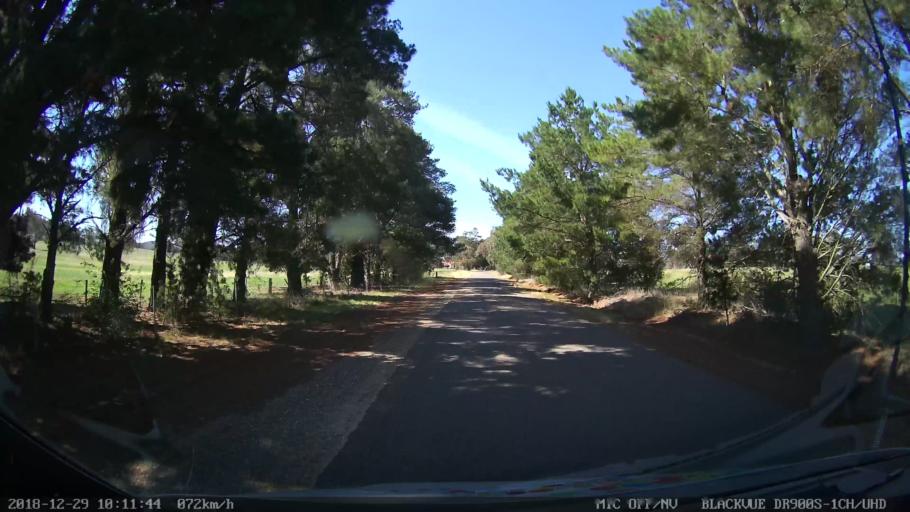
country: AU
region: New South Wales
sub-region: Yass Valley
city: Gundaroo
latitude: -34.8868
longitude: 149.4512
